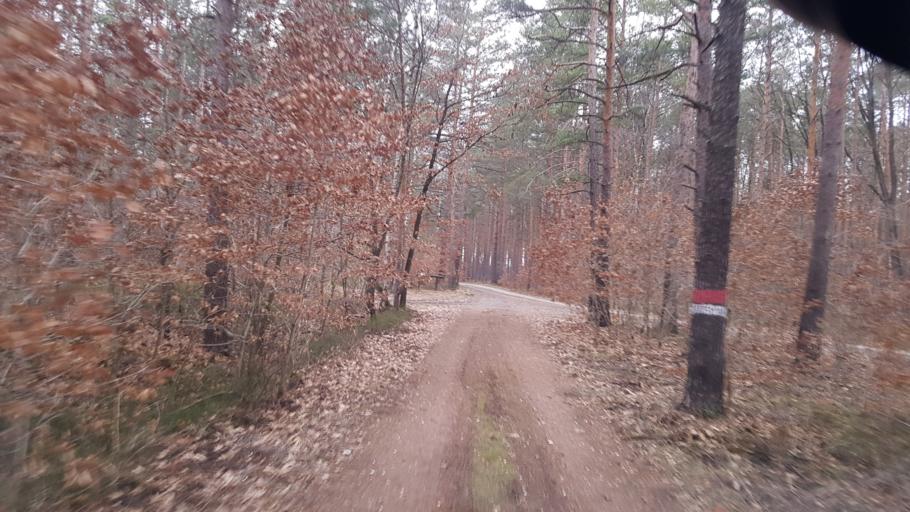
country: DE
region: Brandenburg
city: Trobitz
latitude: 51.6166
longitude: 13.4428
